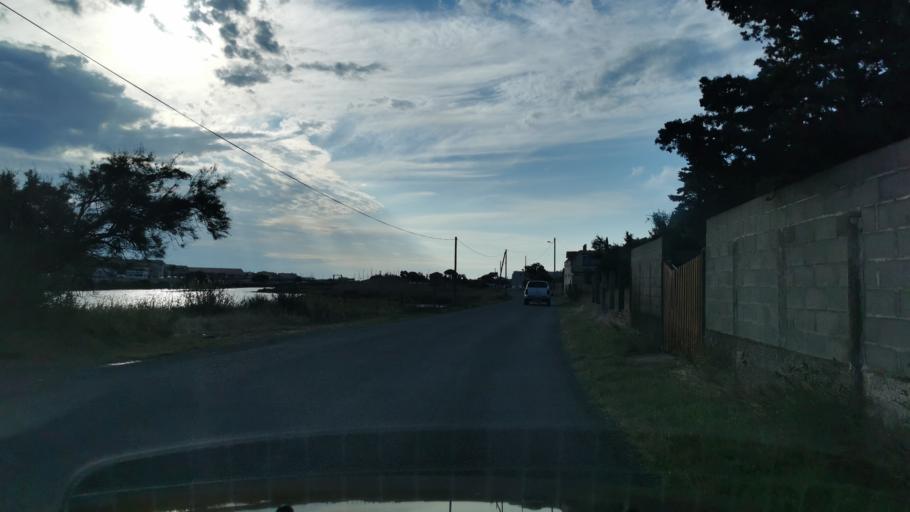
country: FR
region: Languedoc-Roussillon
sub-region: Departement de l'Aude
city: Gruissan
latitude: 43.1064
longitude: 3.0789
